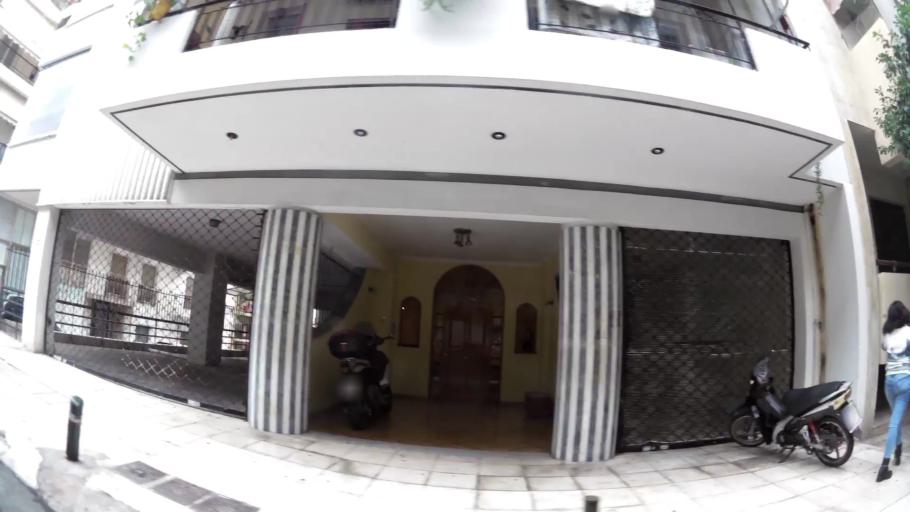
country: GR
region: Attica
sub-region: Nomos Attikis
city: Piraeus
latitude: 37.9306
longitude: 23.6433
